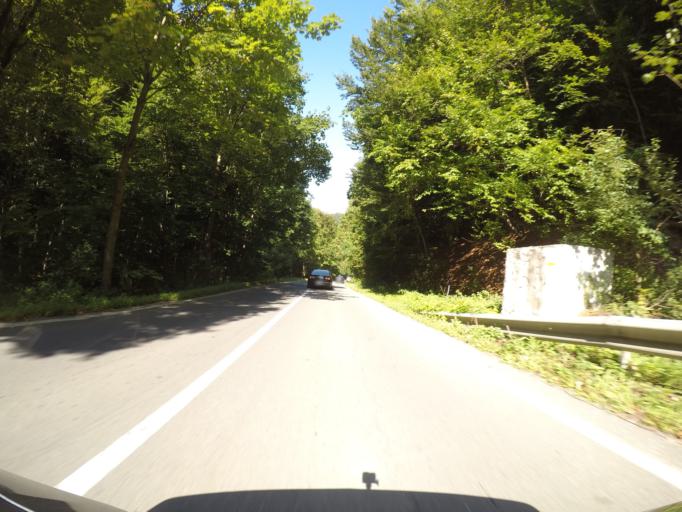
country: RO
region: Brasov
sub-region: Comuna Cristian
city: Cristian
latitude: 45.5860
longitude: 25.5044
